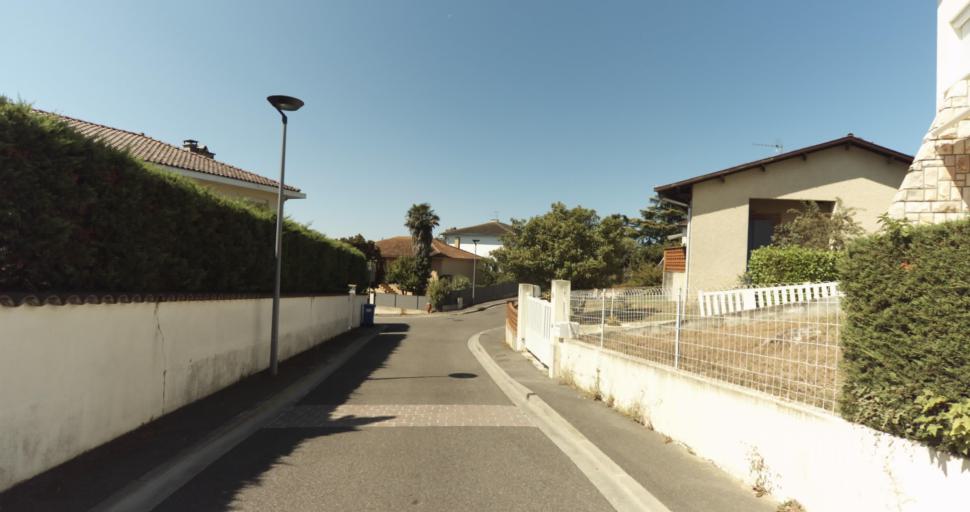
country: FR
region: Midi-Pyrenees
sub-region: Departement de la Haute-Garonne
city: L'Union
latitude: 43.6531
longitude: 1.4892
